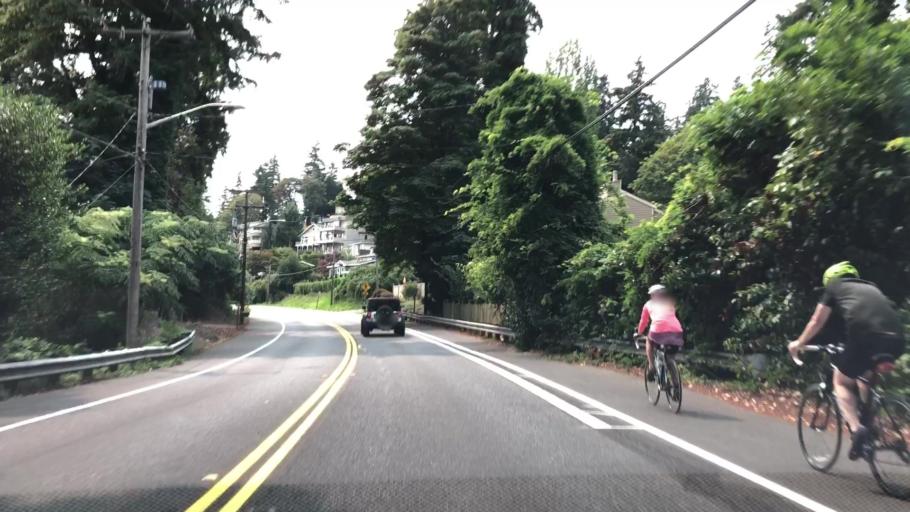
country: US
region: Washington
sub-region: King County
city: Inglewood-Finn Hill
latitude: 47.7026
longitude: -122.2257
